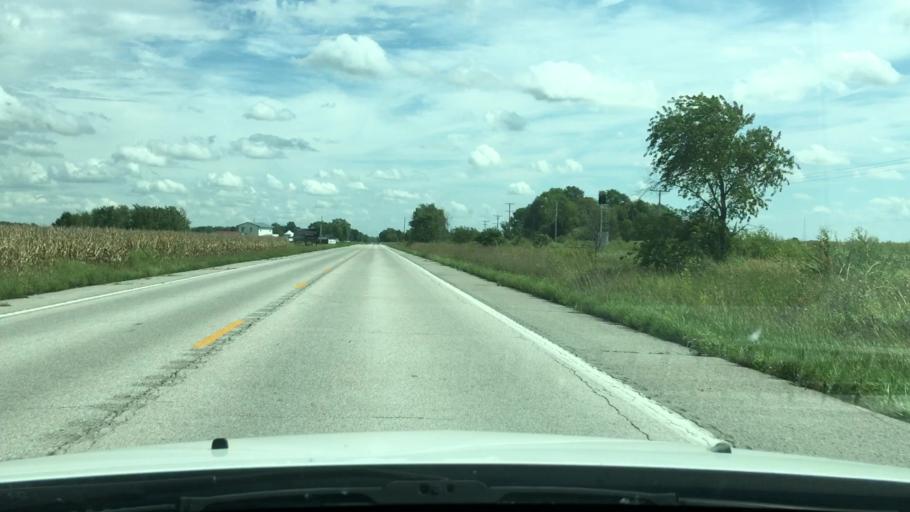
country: US
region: Missouri
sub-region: Audrain County
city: Vandalia
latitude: 39.2906
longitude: -91.5345
